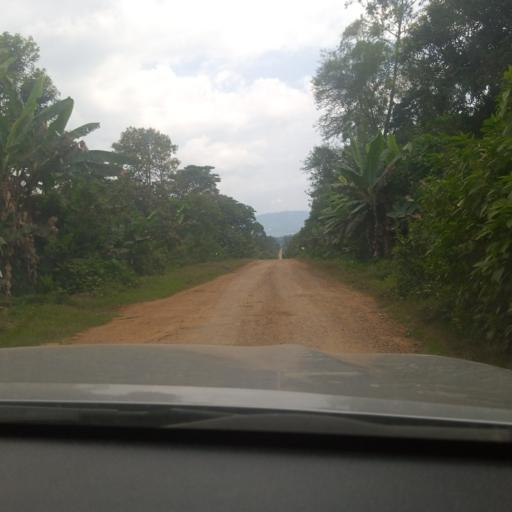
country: ET
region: Southern Nations, Nationalities, and People's Region
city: Tippi
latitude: 7.1412
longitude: 35.4188
